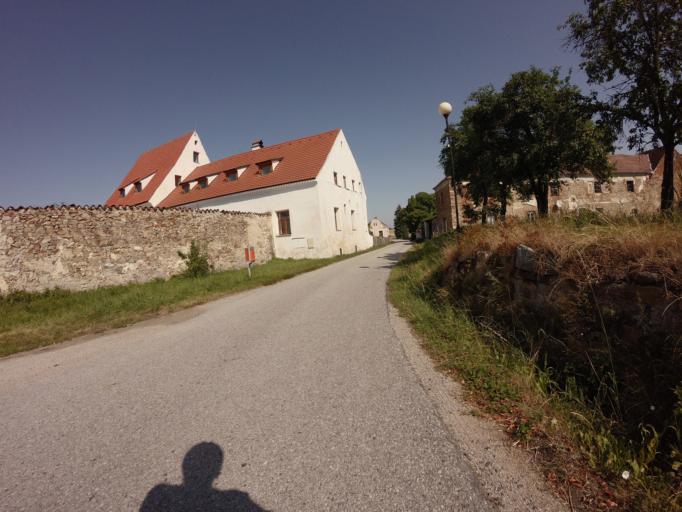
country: CZ
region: Jihocesky
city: Kamenny Ujezd
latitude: 48.8654
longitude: 14.3788
